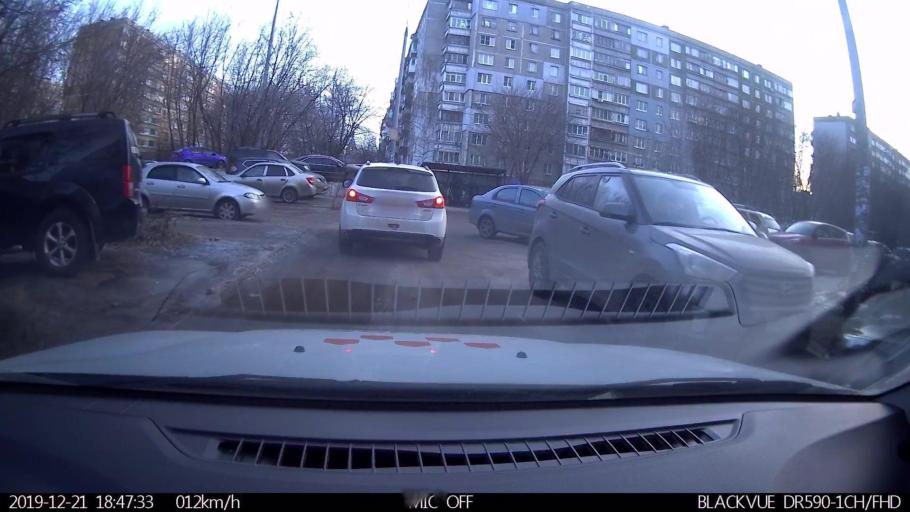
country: RU
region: Nizjnij Novgorod
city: Nizhniy Novgorod
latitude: 56.3279
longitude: 43.9282
